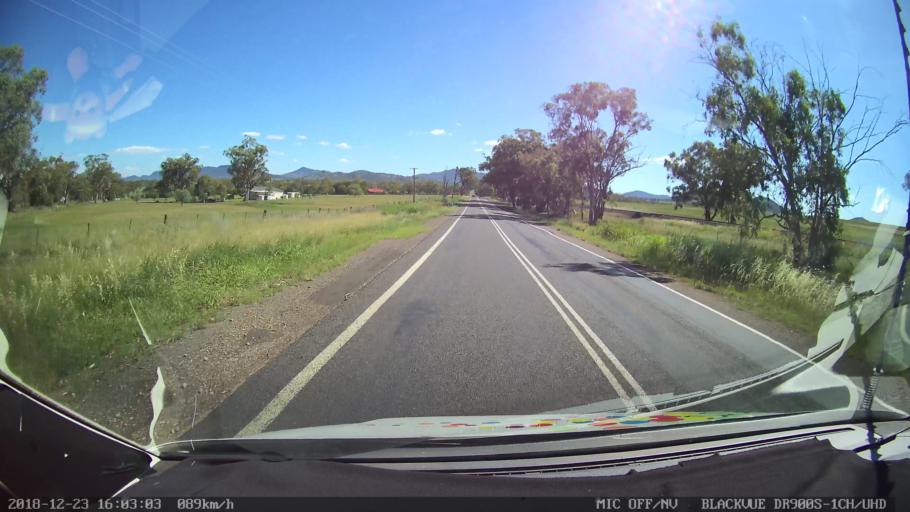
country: AU
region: New South Wales
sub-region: Tamworth Municipality
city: Phillip
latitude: -31.2390
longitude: 150.8040
